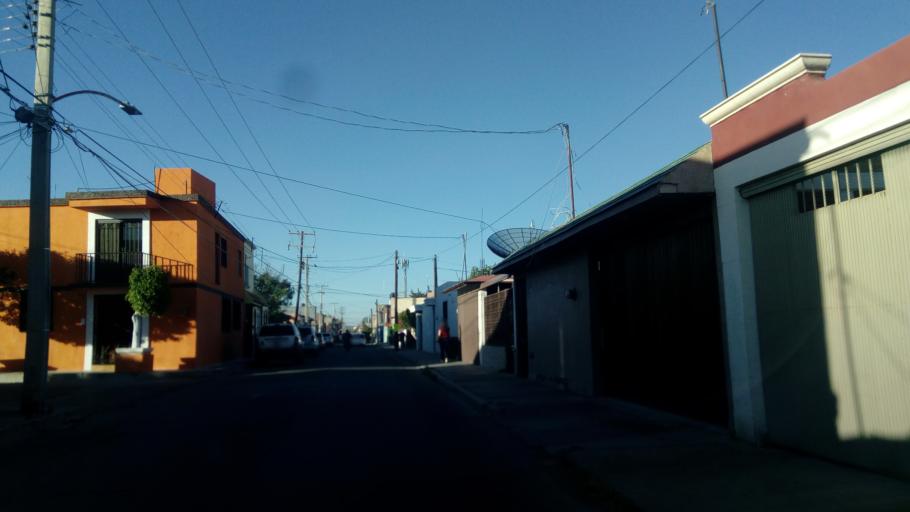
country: MX
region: Durango
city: Victoria de Durango
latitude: 24.0099
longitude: -104.6709
